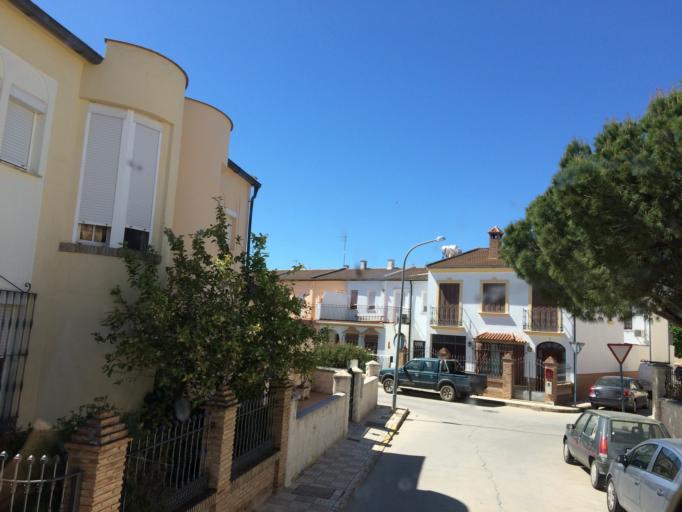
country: ES
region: Andalusia
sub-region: Provincia de Malaga
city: Campillos
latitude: 37.0462
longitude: -4.8680
